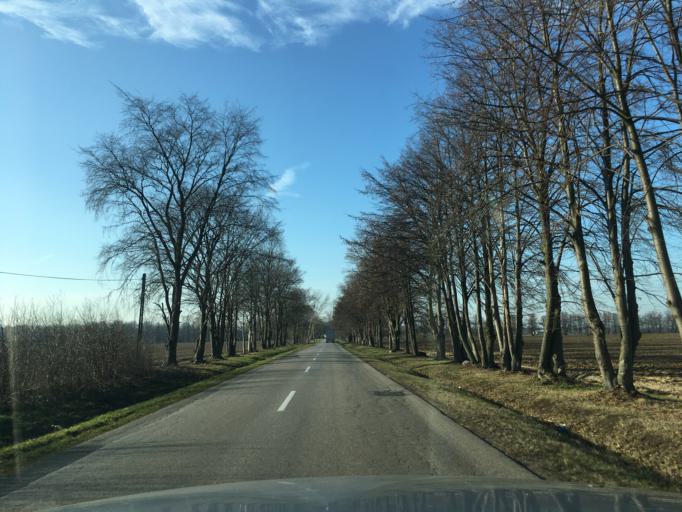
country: PL
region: Masovian Voivodeship
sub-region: Powiat pruszkowski
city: Nadarzyn
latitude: 52.0454
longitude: 20.7965
